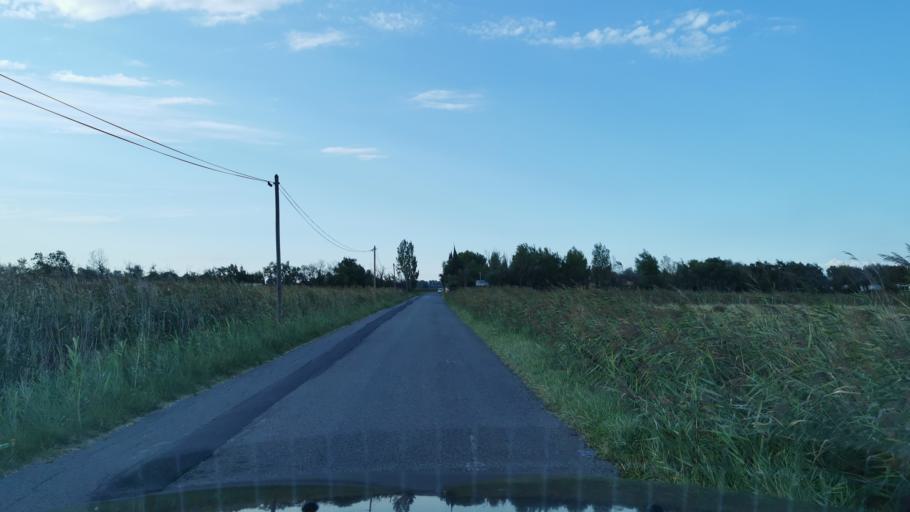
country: FR
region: Languedoc-Roussillon
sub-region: Departement de l'Aude
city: Narbonne
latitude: 43.1396
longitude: 3.0269
